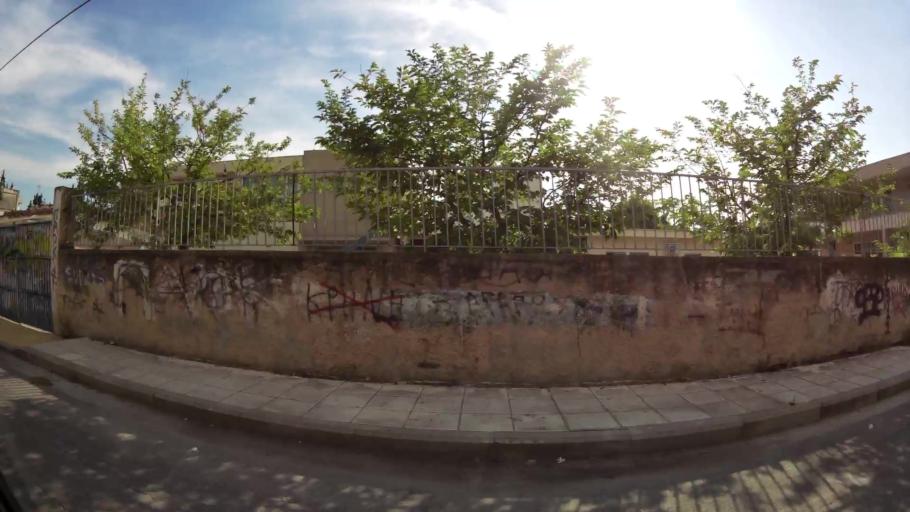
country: GR
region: Central Macedonia
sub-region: Nomos Thessalonikis
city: Kalamaria
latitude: 40.5713
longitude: 22.9748
